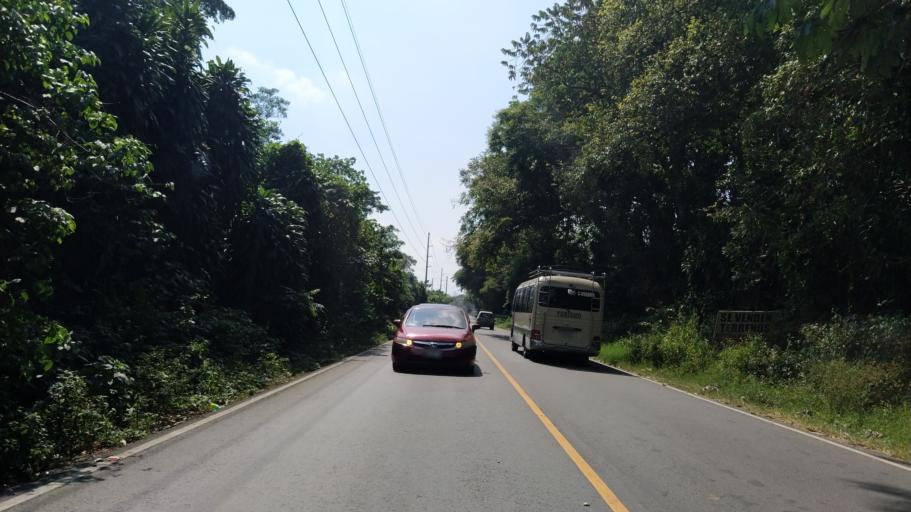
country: GT
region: Quetzaltenango
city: El Palmar
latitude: 14.6321
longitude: -91.5854
